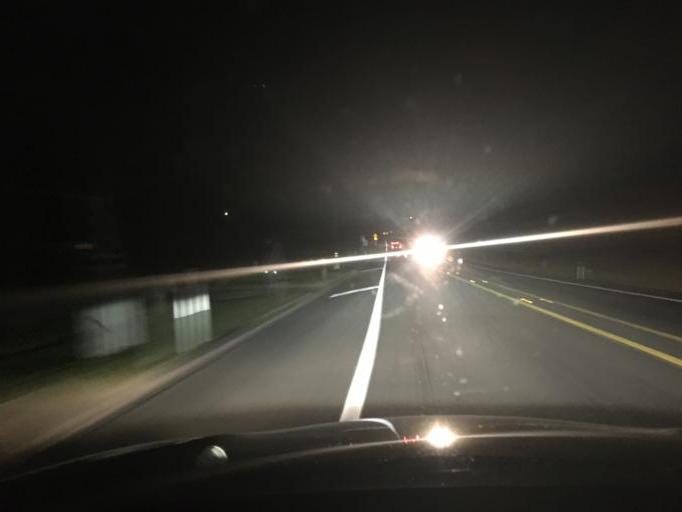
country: NZ
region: Waikato
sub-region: Hamilton City
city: Hamilton
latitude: -37.8435
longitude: 175.3060
